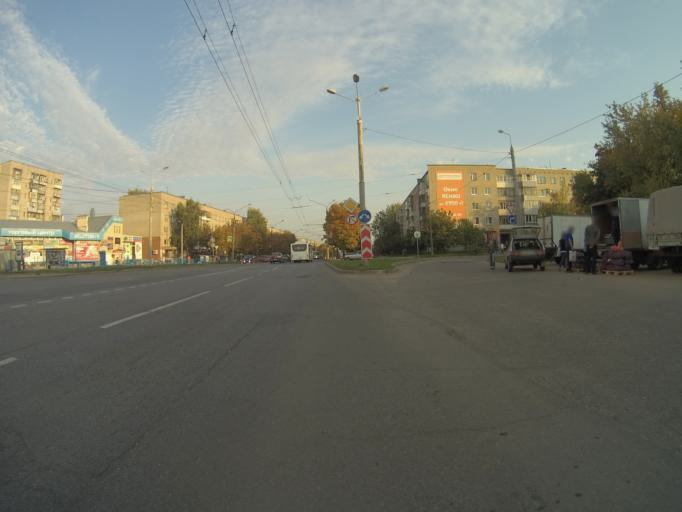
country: RU
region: Vladimir
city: Bogolyubovo
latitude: 56.1693
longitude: 40.4766
